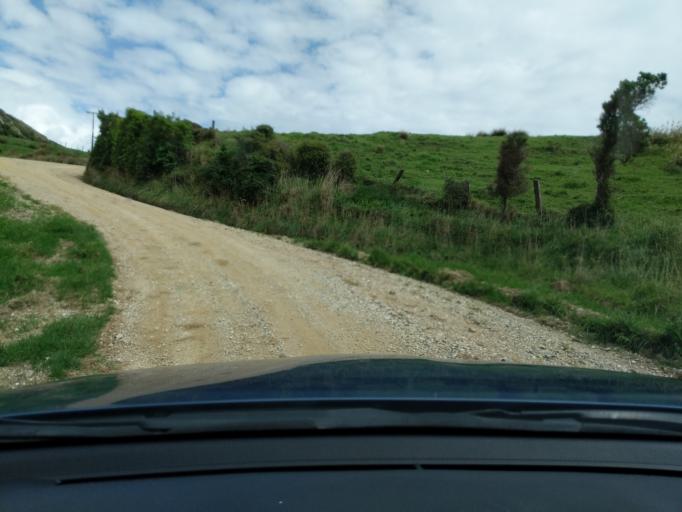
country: NZ
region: Tasman
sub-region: Tasman District
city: Takaka
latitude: -40.6589
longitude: 172.4156
